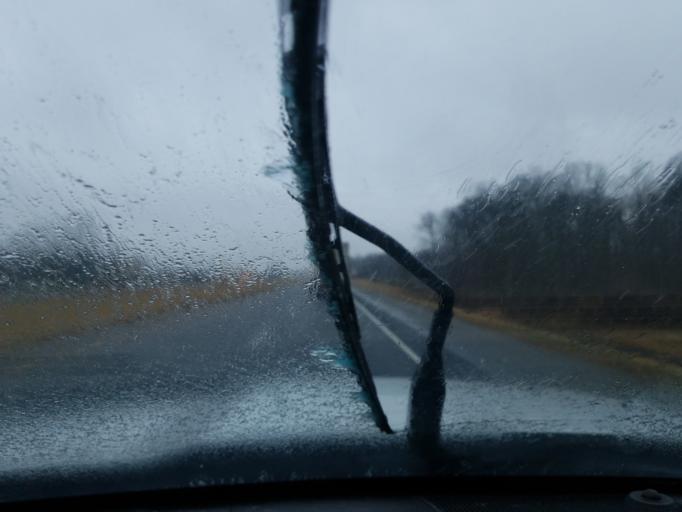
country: US
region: Indiana
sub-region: Huntington County
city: Roanoke
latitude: 40.9815
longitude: -85.2759
